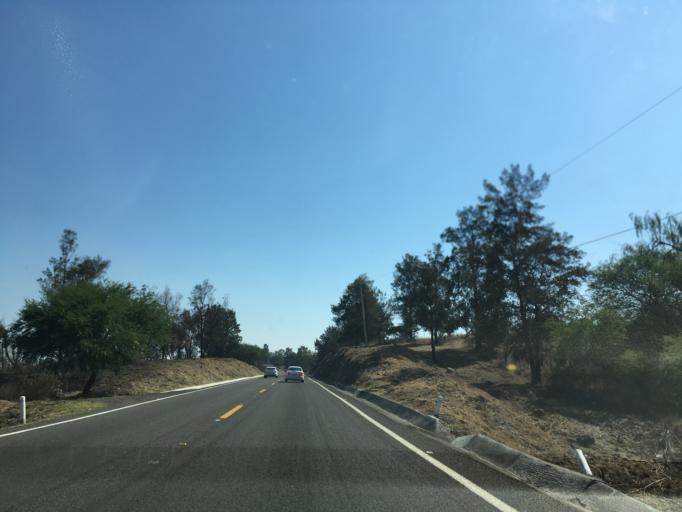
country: MX
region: Michoacan
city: Charo
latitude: 19.7706
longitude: -101.0183
